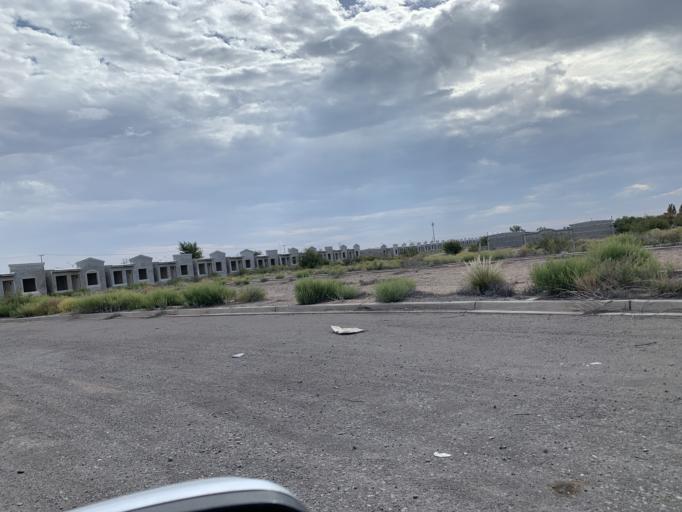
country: US
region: Texas
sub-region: El Paso County
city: San Elizario
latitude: 31.5823
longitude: -106.3359
